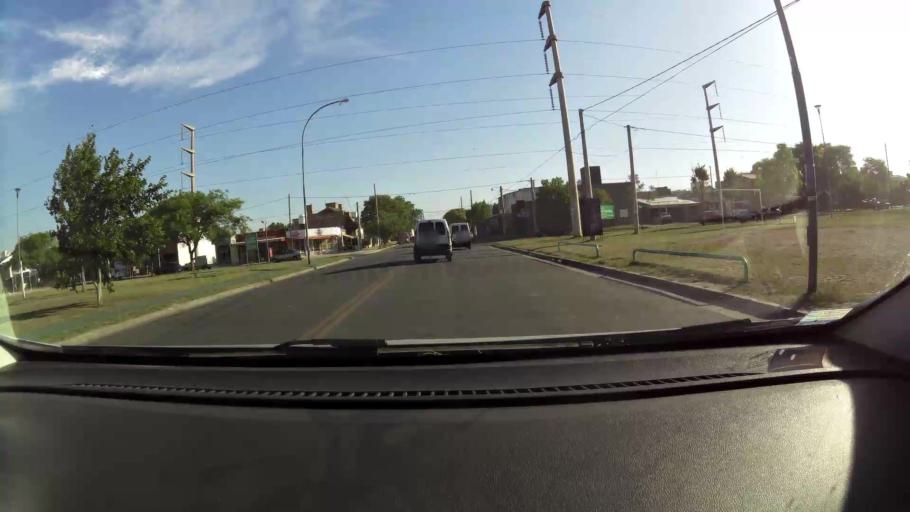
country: AR
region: Cordoba
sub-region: Departamento de Capital
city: Cordoba
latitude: -31.3583
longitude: -64.2130
